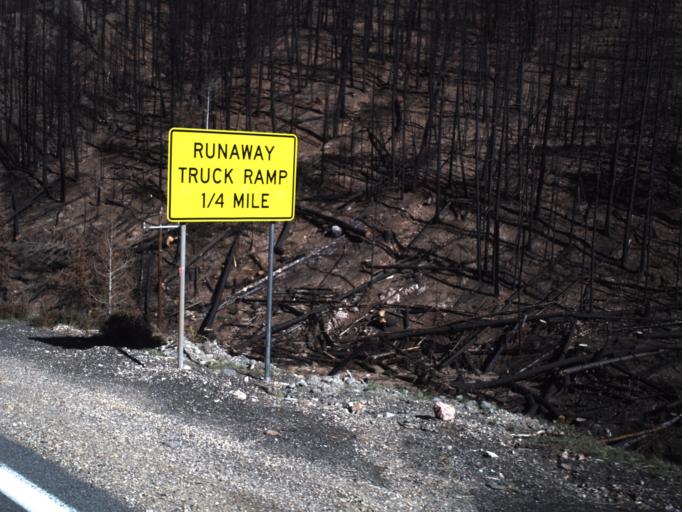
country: US
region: Utah
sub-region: Iron County
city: Parowan
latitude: 37.7261
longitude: -112.8411
